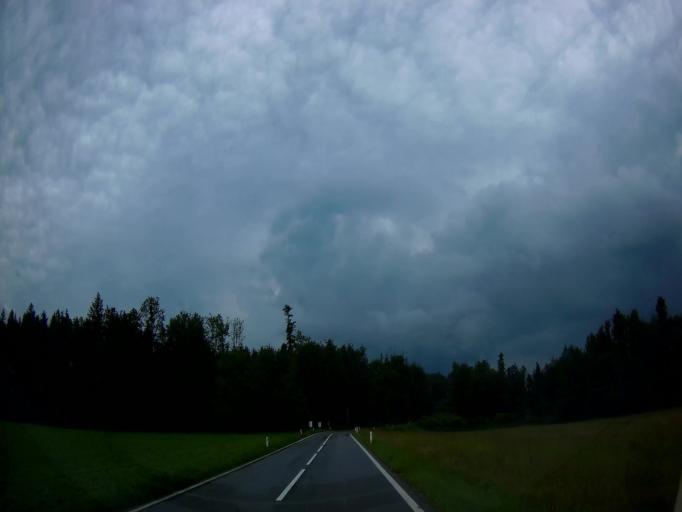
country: AT
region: Salzburg
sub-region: Politischer Bezirk Salzburg-Umgebung
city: Mattsee
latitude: 48.0375
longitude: 13.1467
